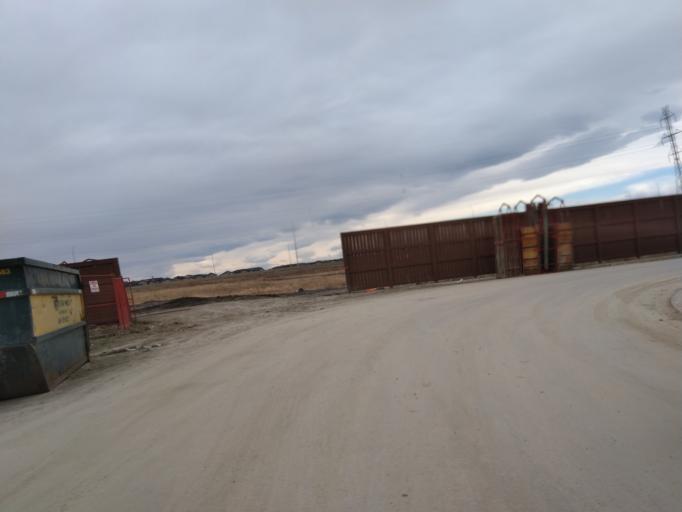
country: CA
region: Alberta
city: Calgary
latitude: 51.1770
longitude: -114.0871
